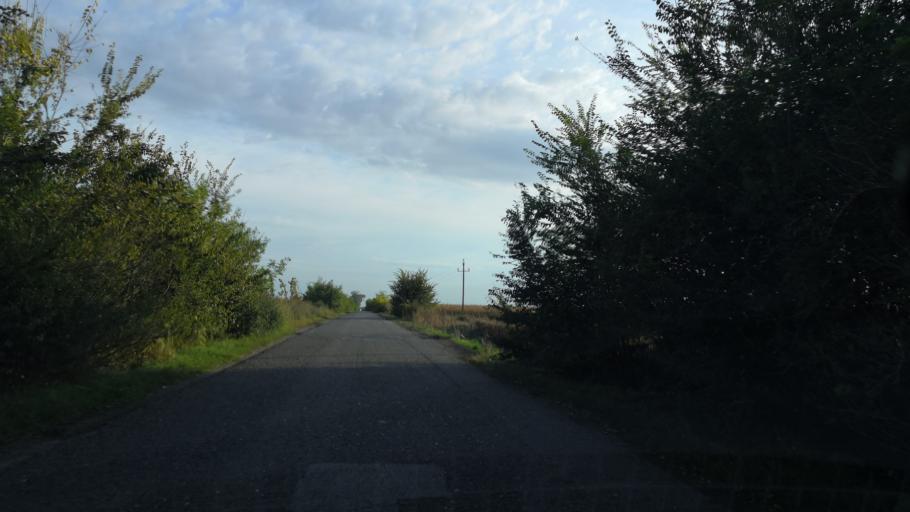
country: RS
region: Autonomna Pokrajina Vojvodina
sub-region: Sremski Okrug
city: Stara Pazova
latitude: 45.0226
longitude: 20.1703
